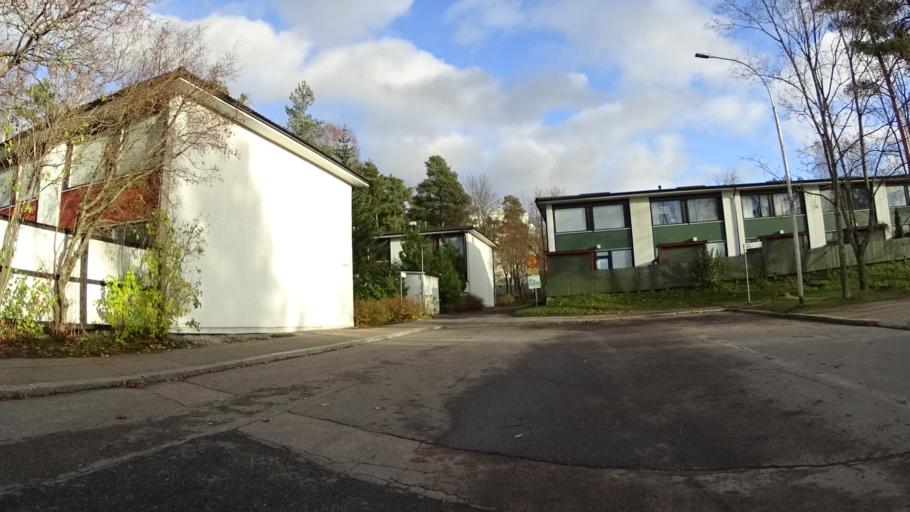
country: FI
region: Uusimaa
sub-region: Helsinki
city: Vantaa
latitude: 60.3060
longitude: 25.0192
